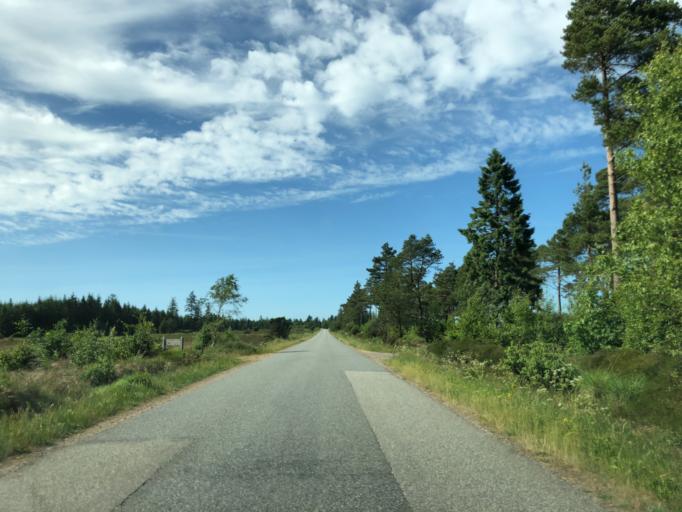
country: DK
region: Central Jutland
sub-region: Herning Kommune
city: Kibaek
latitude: 56.0588
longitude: 8.9203
